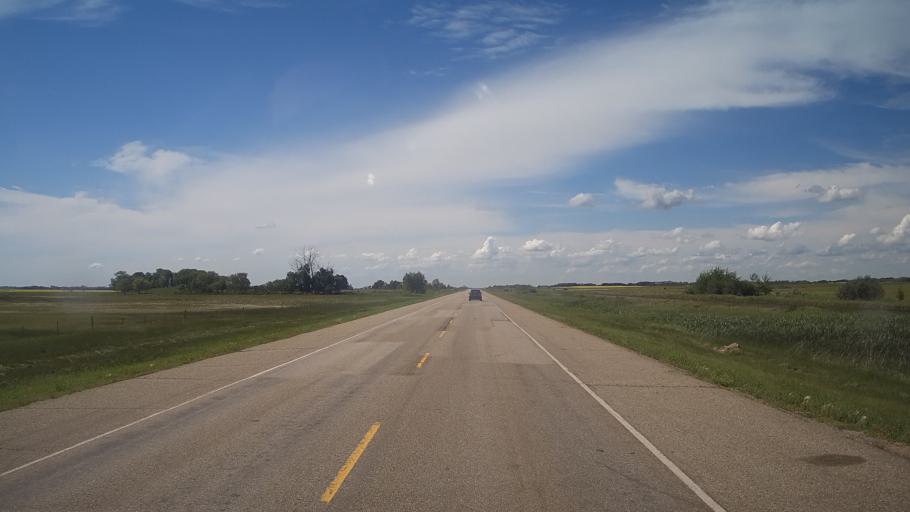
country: CA
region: Saskatchewan
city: Yorkton
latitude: 51.0665
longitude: -102.2169
